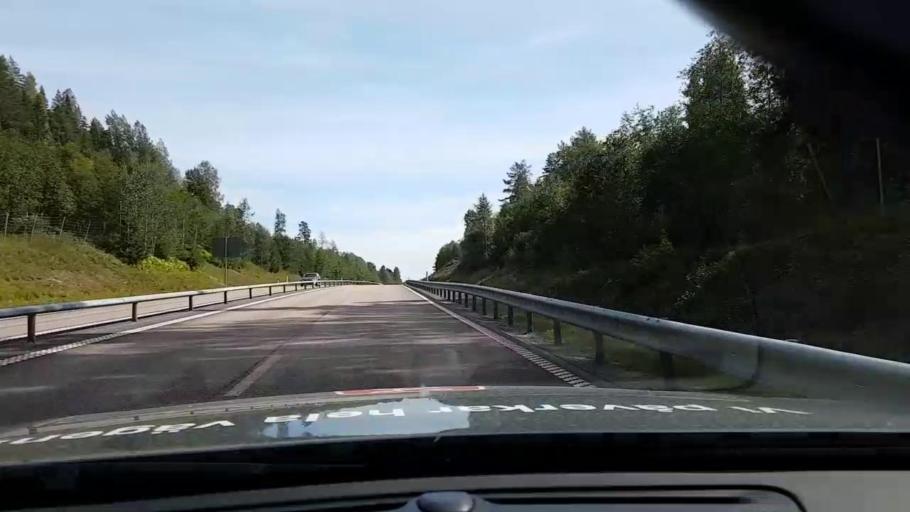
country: SE
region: Vaesternorrland
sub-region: OErnskoeldsviks Kommun
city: Ornskoldsvik
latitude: 63.3150
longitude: 18.8104
